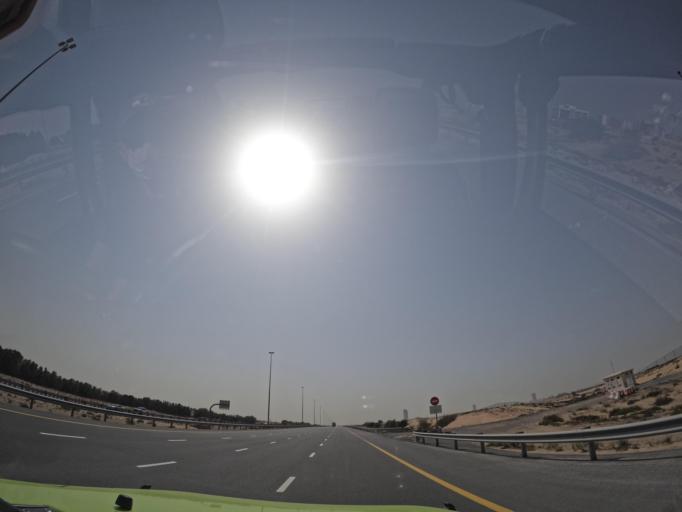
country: AE
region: Dubai
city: Dubai
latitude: 25.0938
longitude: 55.3601
